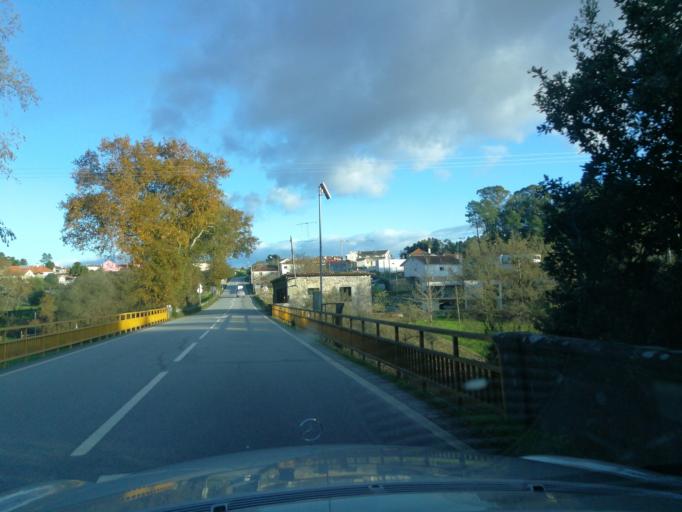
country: PT
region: Braga
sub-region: Esposende
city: Marinhas
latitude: 41.6162
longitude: -8.7525
